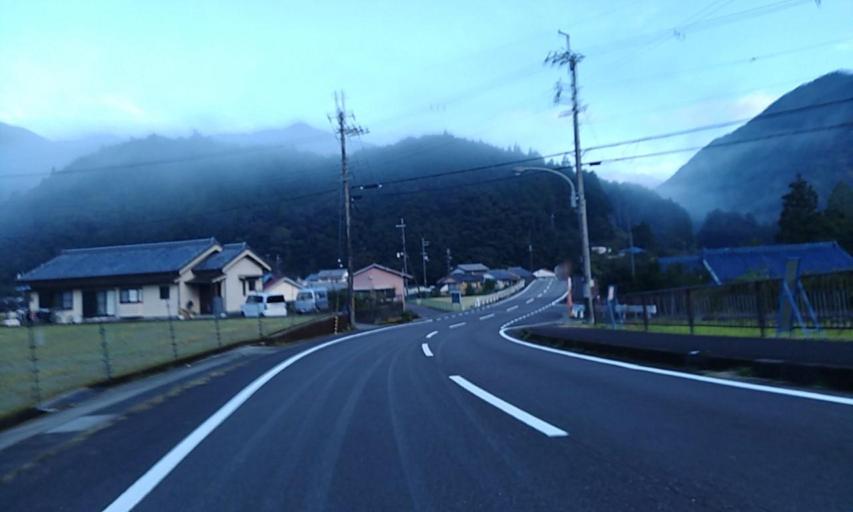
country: JP
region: Wakayama
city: Shingu
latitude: 33.7283
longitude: 135.9101
